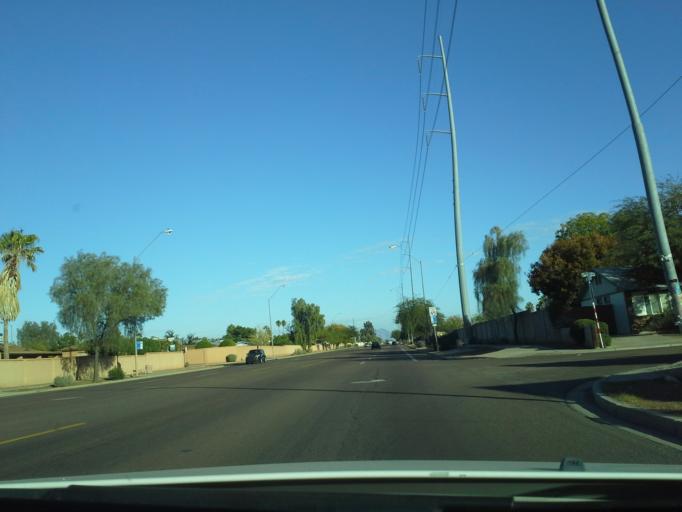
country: US
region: Arizona
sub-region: Maricopa County
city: Glendale
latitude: 33.6546
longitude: -112.1304
